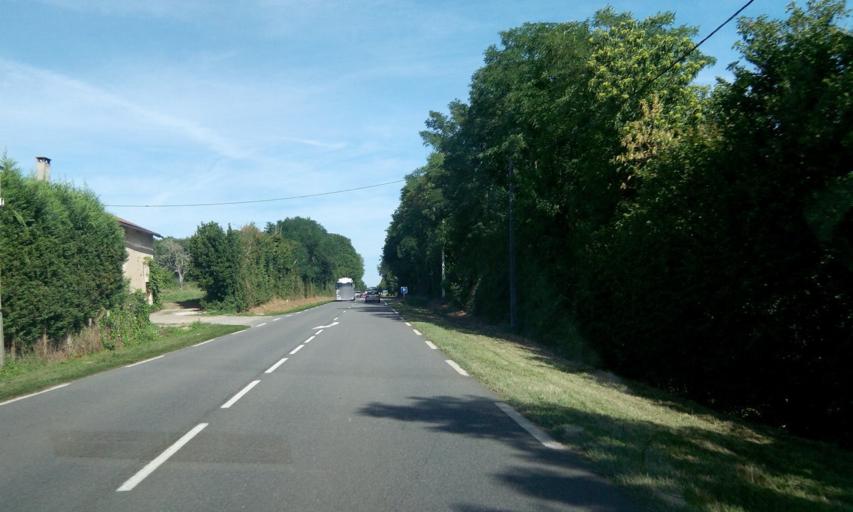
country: FR
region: Poitou-Charentes
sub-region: Departement de la Charente
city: Confolens
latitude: 45.9851
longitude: 0.6779
